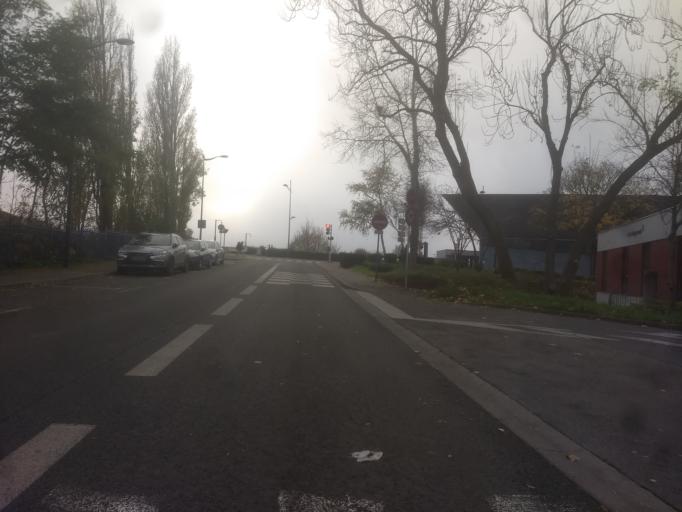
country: FR
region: Nord-Pas-de-Calais
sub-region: Departement du Pas-de-Calais
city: Arras
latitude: 50.2857
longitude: 2.7787
